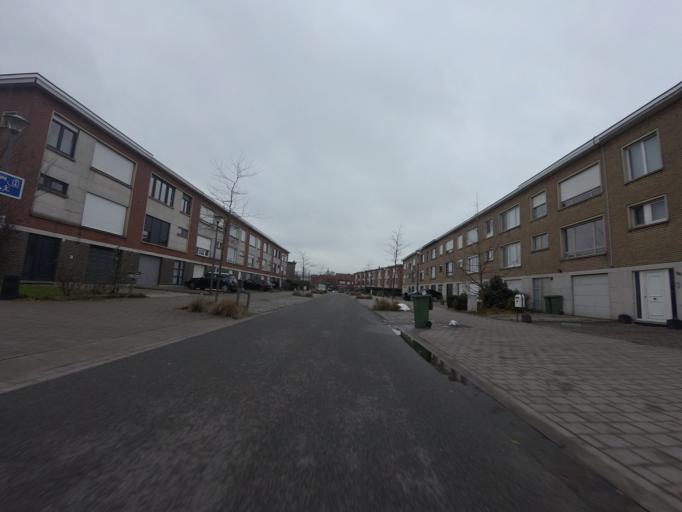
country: BE
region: Flanders
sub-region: Provincie Antwerpen
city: Hoboken
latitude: 51.1608
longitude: 4.3483
